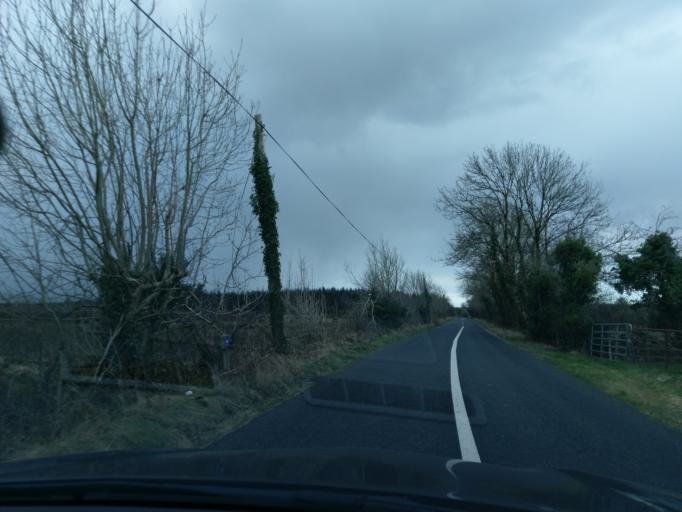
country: IE
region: Connaught
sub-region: County Galway
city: Athenry
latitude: 53.3985
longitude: -8.6259
